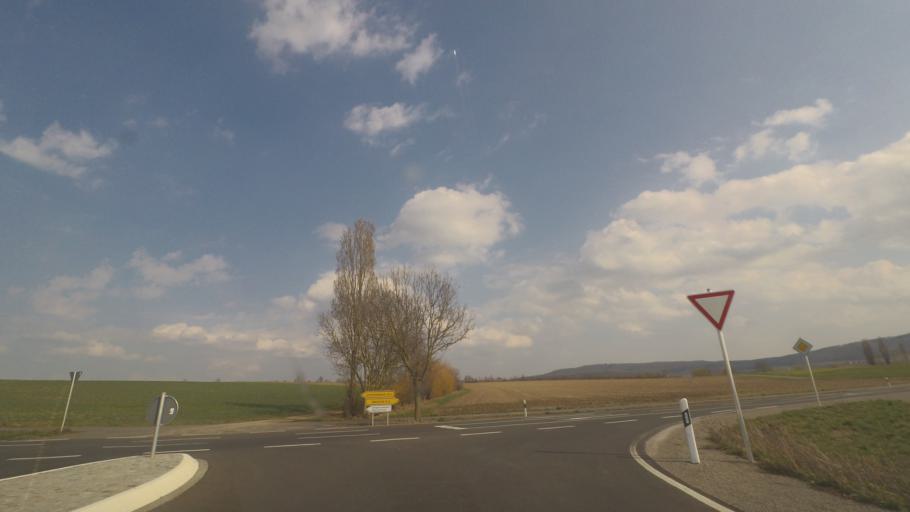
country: DE
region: Bavaria
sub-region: Regierungsbezirk Unterfranken
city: Wiesentheid
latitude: 49.7807
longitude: 10.3579
